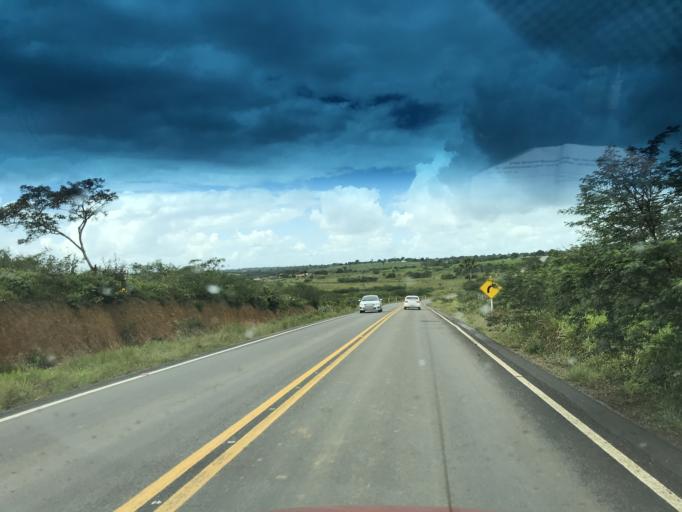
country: BR
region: Bahia
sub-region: Conceicao Do Almeida
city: Conceicao do Almeida
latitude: -12.6794
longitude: -39.2579
